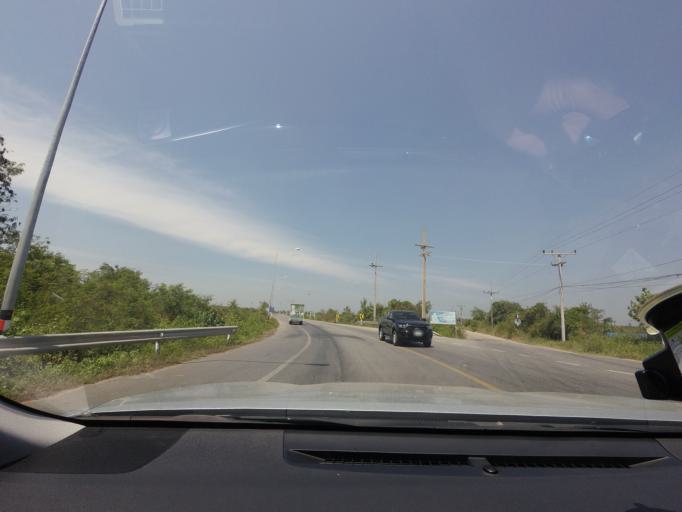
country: TH
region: Surat Thani
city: Tha Chang
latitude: 9.2219
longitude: 99.2196
